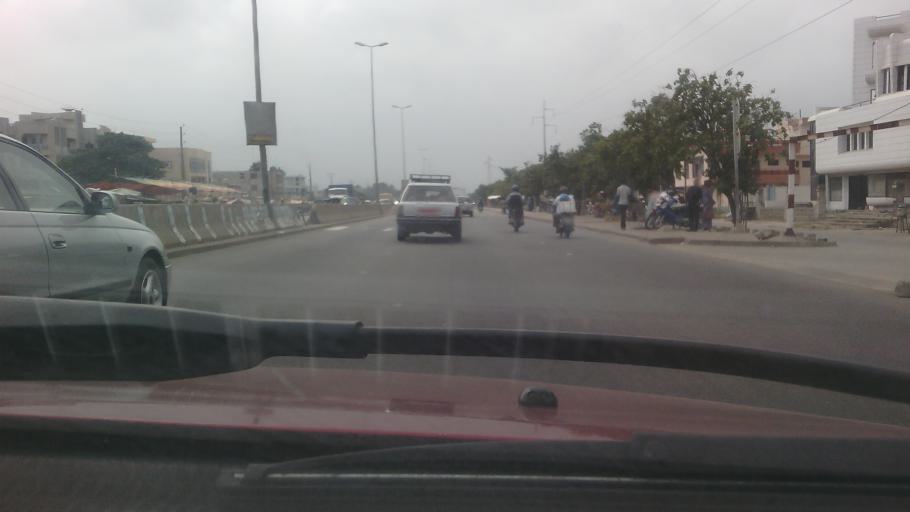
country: BJ
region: Littoral
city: Cotonou
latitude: 6.3694
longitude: 2.4907
